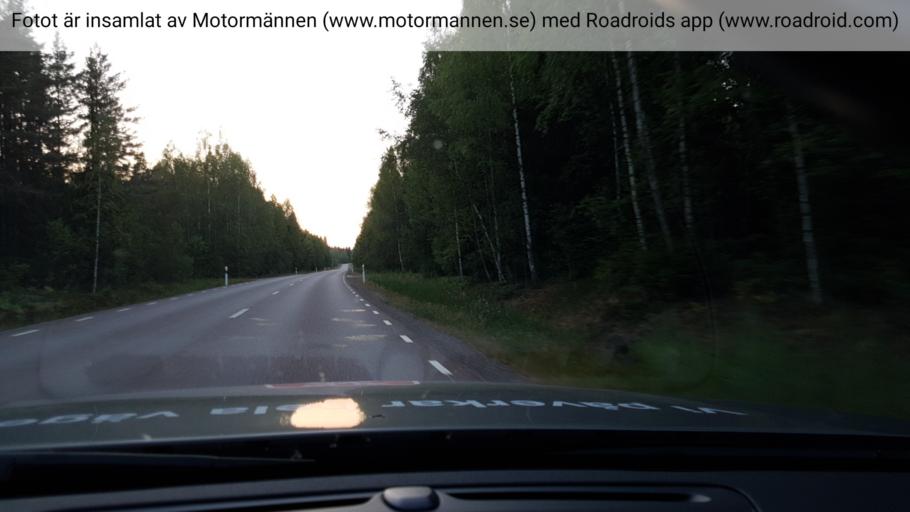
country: SE
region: Uppsala
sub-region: Heby Kommun
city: OEstervala
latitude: 60.0532
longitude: 17.2289
